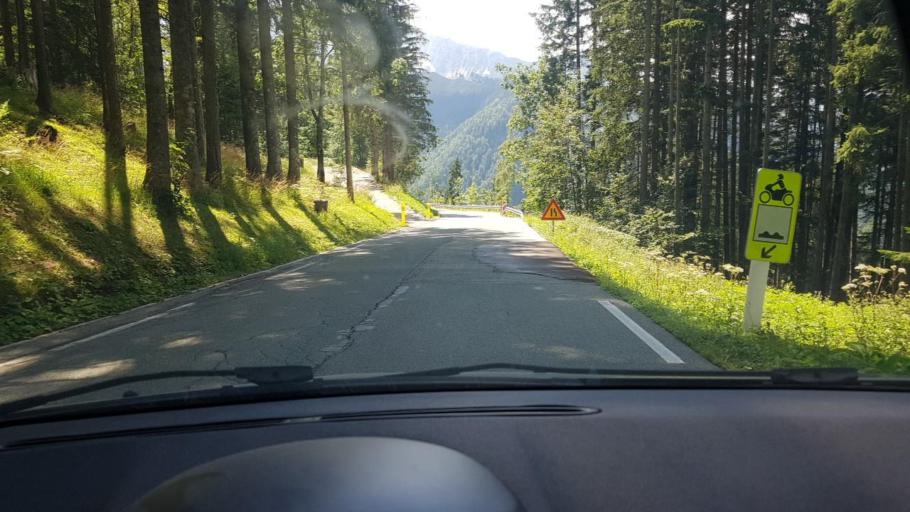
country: SI
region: Jezersko
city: Zgornje Jezersko
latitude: 46.4111
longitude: 14.5307
